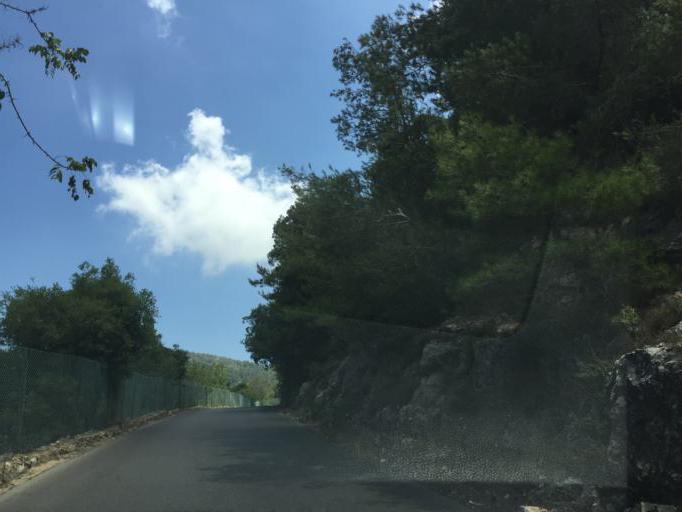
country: LB
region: Mont-Liban
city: Beit ed Dine
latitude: 33.6944
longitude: 35.5749
